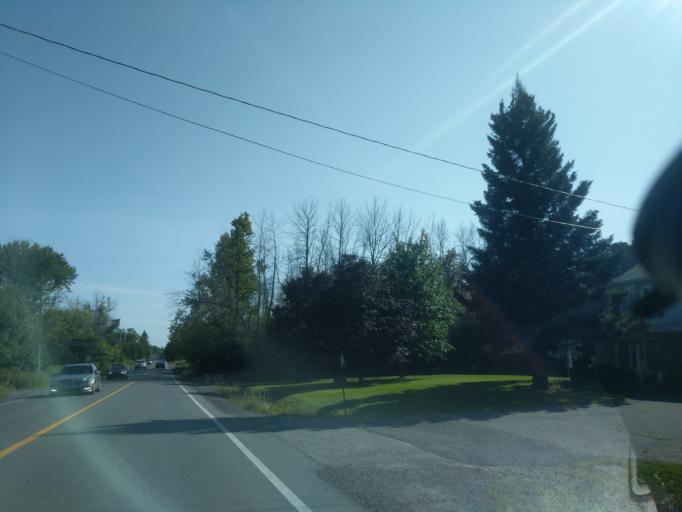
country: CA
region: Ontario
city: Bells Corners
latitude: 45.4117
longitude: -75.8083
